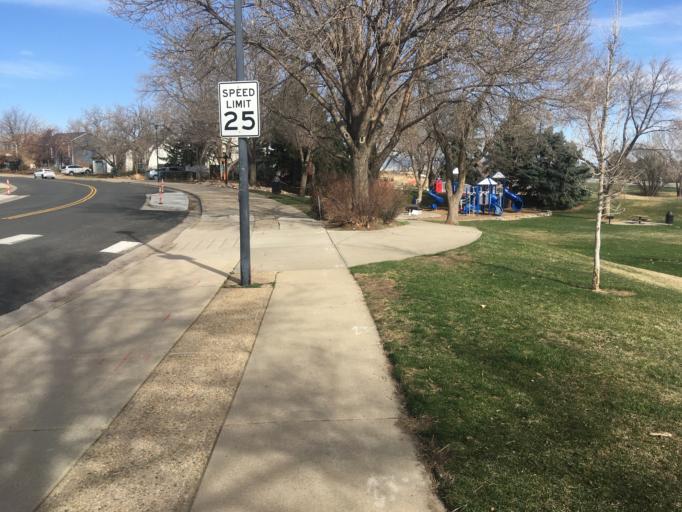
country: US
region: Colorado
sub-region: Boulder County
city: Lafayette
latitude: 40.0104
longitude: -105.0969
